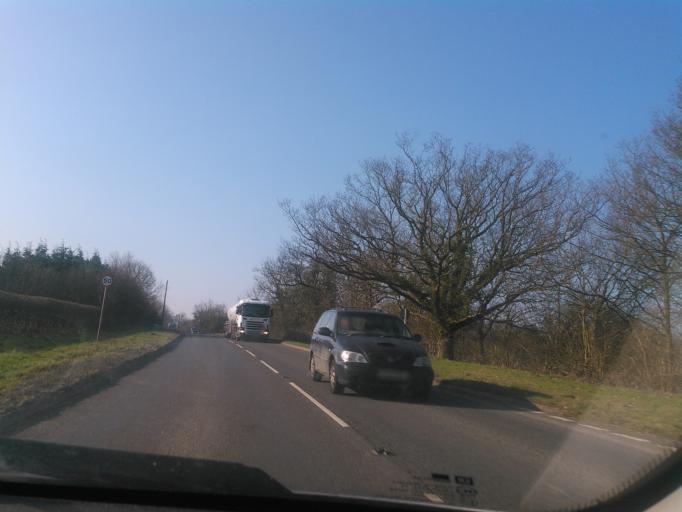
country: GB
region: England
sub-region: Shropshire
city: Longnor
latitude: 52.5776
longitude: -2.7784
